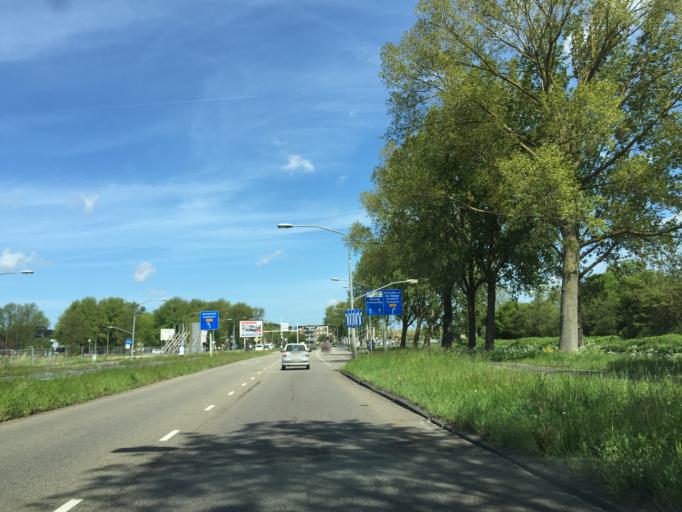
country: NL
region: North Holland
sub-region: Gemeente Haarlem
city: Haarlem
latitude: 52.3684
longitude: 4.6544
